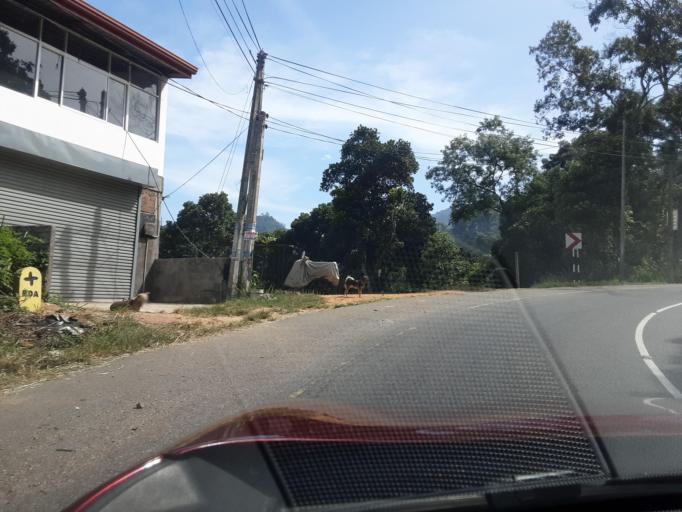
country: LK
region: Uva
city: Badulla
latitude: 6.9850
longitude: 81.0757
